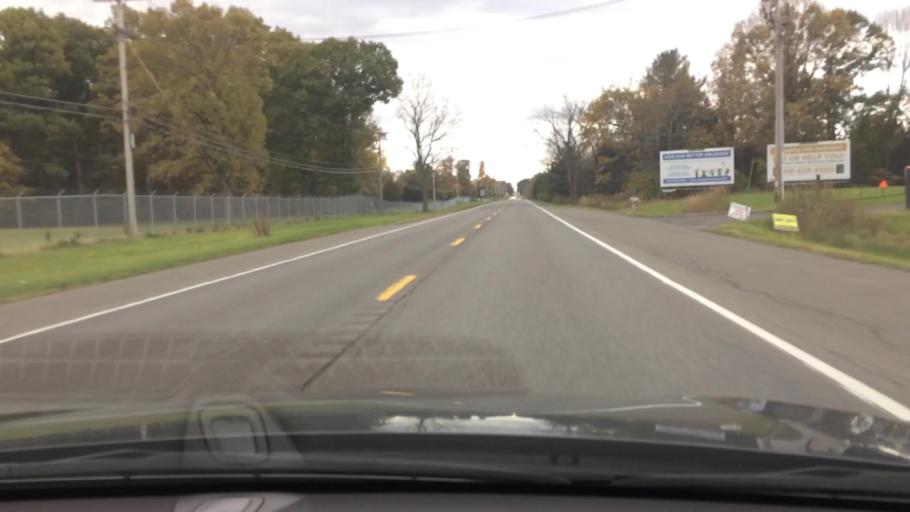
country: US
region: New York
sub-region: Columbia County
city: Stottville
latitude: 42.2944
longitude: -73.7140
